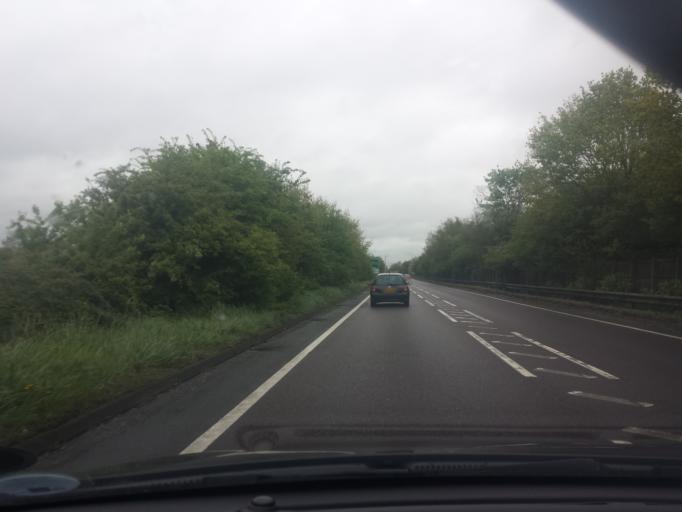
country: GB
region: England
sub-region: Essex
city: Dovercourt
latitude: 51.9365
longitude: 1.2517
